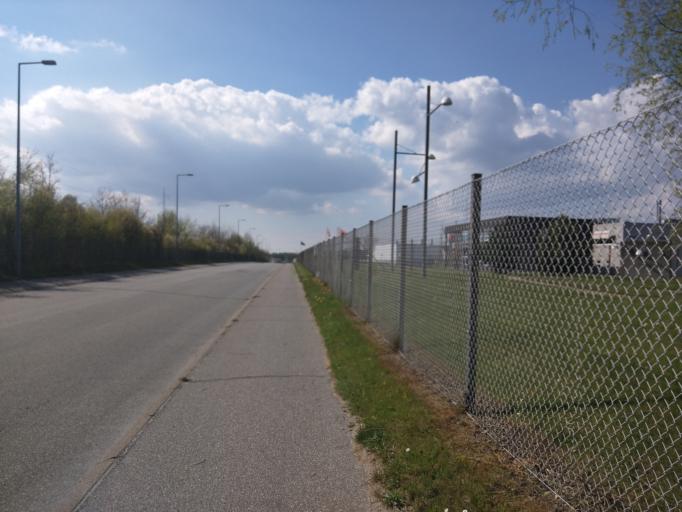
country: DK
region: South Denmark
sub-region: Fredericia Kommune
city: Snoghoj
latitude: 55.5407
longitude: 9.6992
